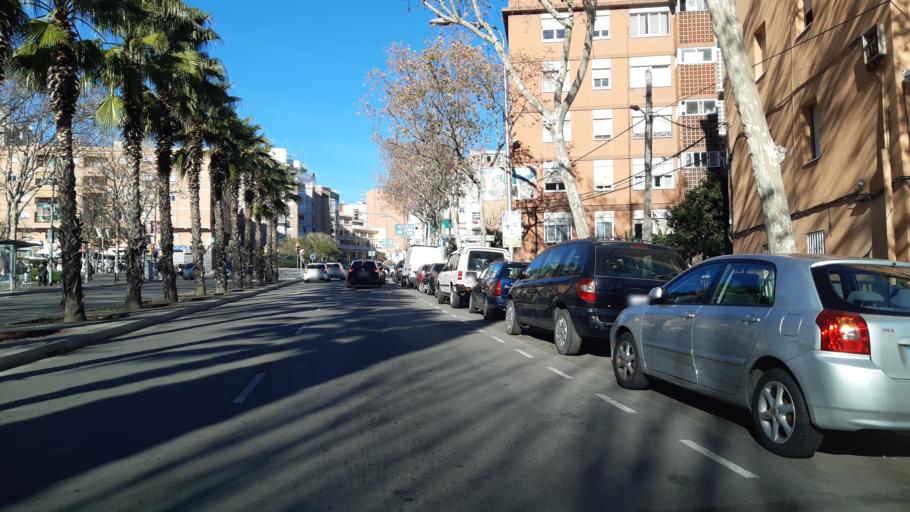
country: ES
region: Catalonia
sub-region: Provincia de Barcelona
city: L'Hospitalet de Llobregat
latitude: 41.3683
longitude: 2.1035
